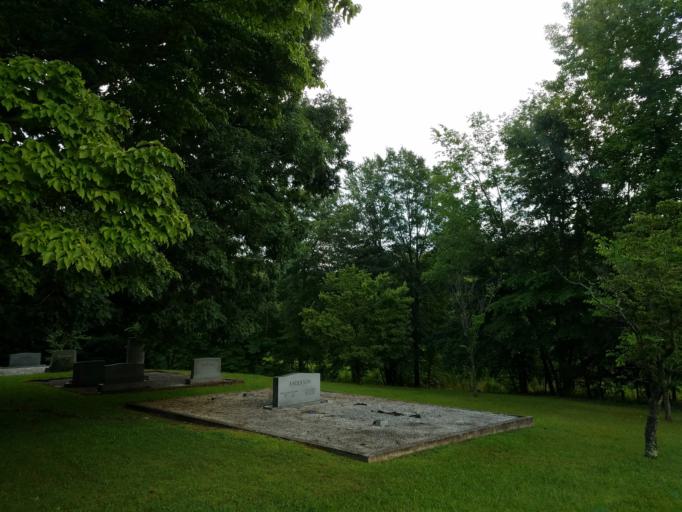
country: US
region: Georgia
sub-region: Fannin County
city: Blue Ridge
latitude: 34.8607
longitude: -84.3247
